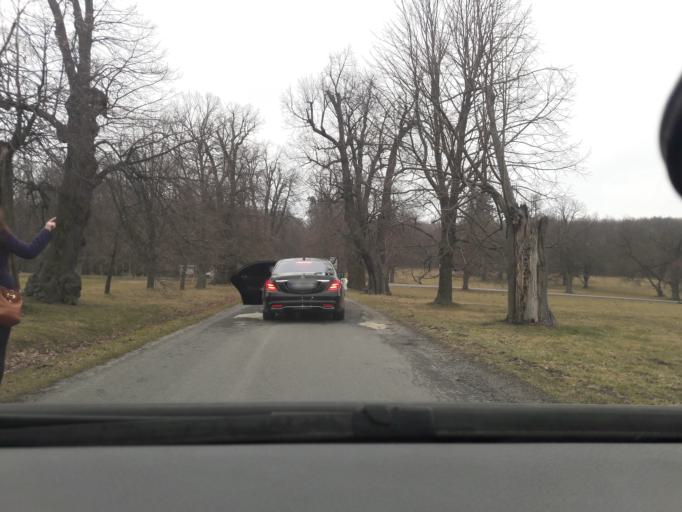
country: SK
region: Bratislavsky
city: Modra
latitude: 48.3947
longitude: 17.3351
